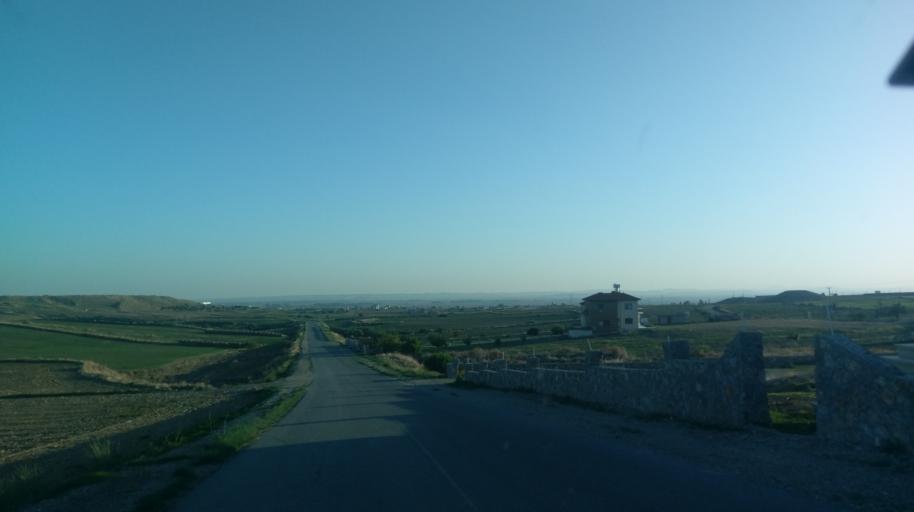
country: CY
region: Ammochostos
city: Lefkonoiko
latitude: 35.2532
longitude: 33.5494
